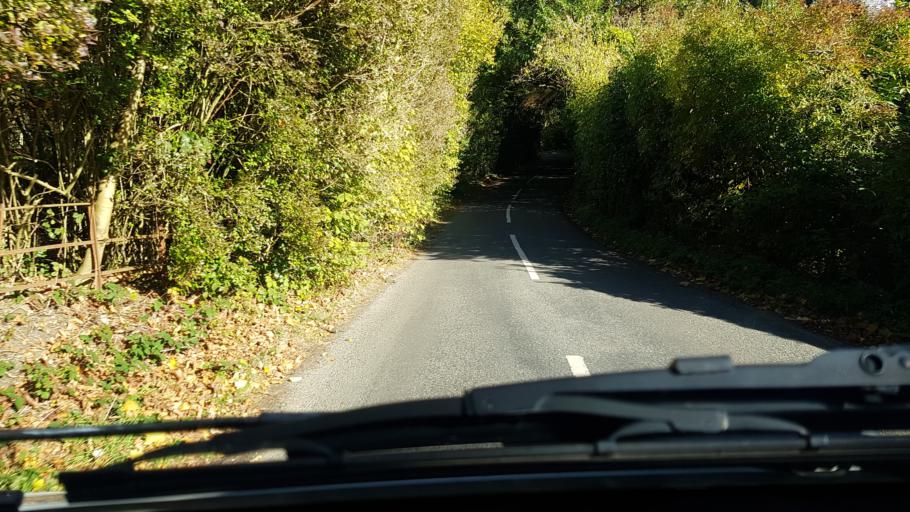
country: GB
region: England
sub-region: Surrey
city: Ockley
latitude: 51.1739
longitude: -0.3592
